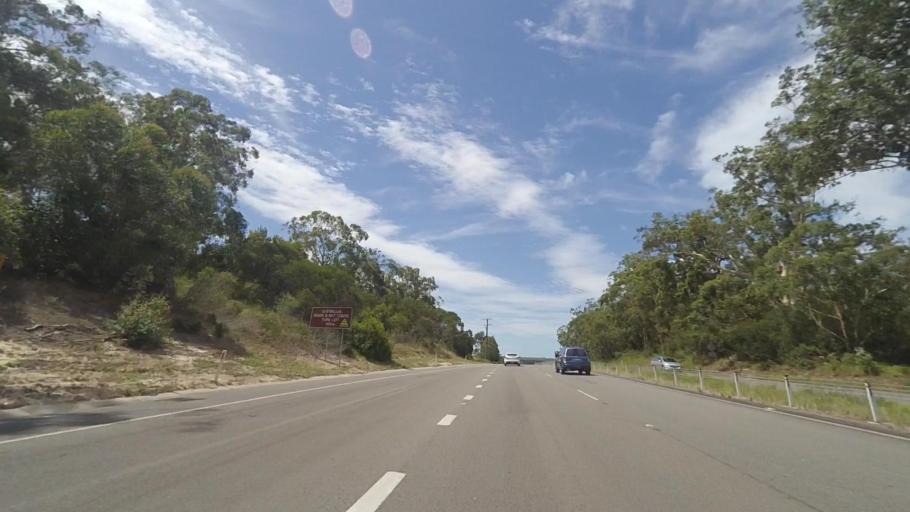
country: AU
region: New South Wales
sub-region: Port Stephens Shire
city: Anna Bay
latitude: -32.7705
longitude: 152.0116
